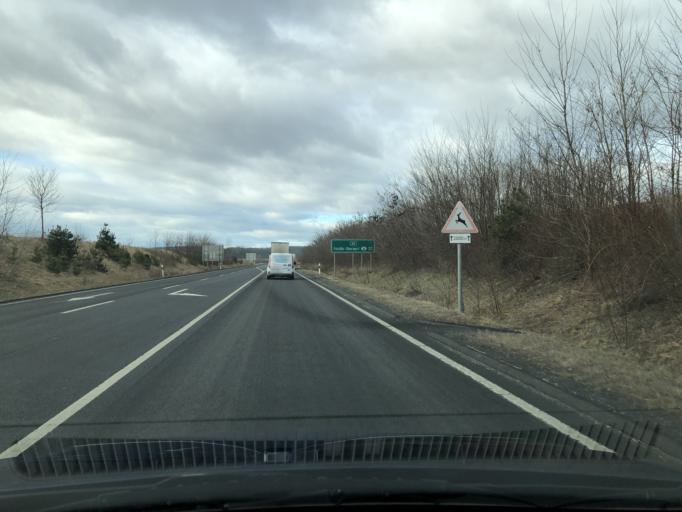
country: AT
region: Burgenland
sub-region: Politischer Bezirk Oberwart
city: Schachendorf
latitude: 47.2469
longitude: 16.4955
